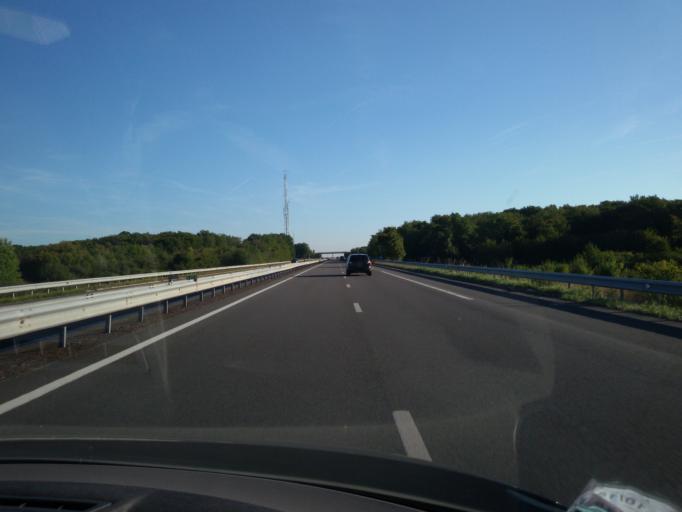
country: FR
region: Centre
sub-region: Departement du Cher
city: Levet
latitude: 46.9128
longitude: 2.4201
